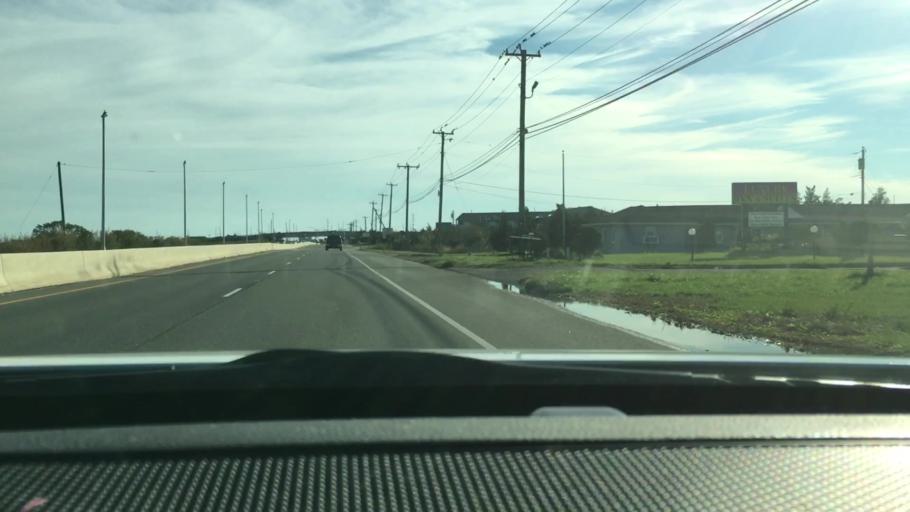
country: US
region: New Jersey
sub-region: Atlantic County
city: Absecon
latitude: 39.4022
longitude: -74.4922
